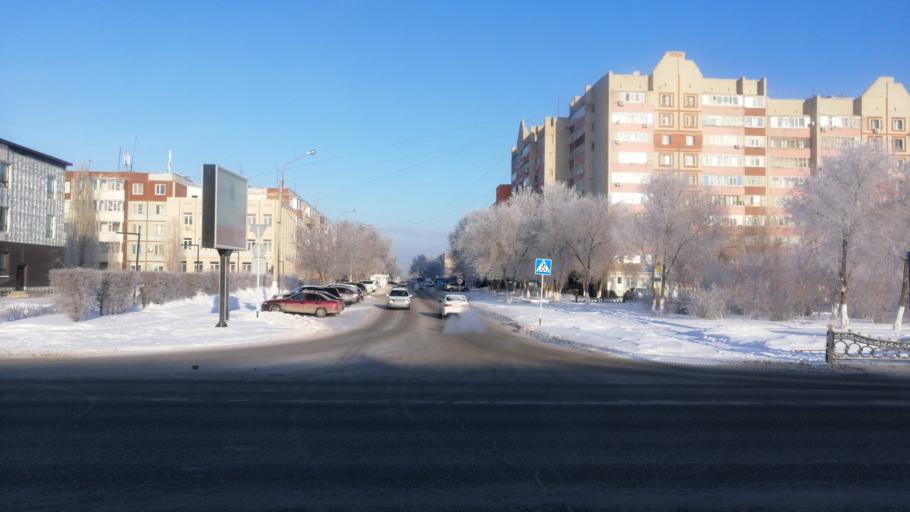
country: KZ
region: Aqtoebe
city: Aqtobe
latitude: 50.2868
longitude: 57.1510
